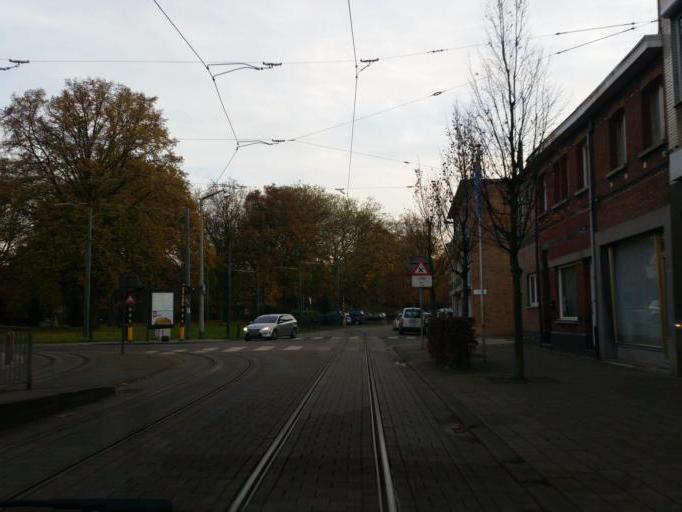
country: BE
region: Flanders
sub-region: Provincie Antwerpen
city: Hoboken
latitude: 51.1739
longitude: 4.3512
